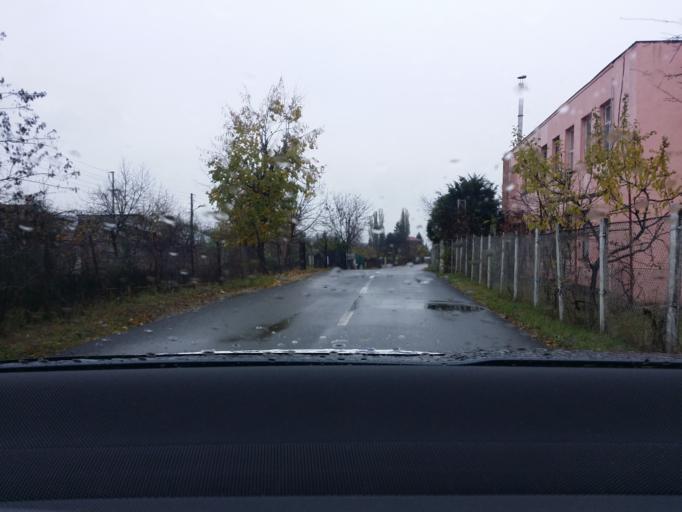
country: RO
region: Prahova
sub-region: Comuna Cornu
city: Cornu de Jos
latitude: 45.1351
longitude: 25.7073
